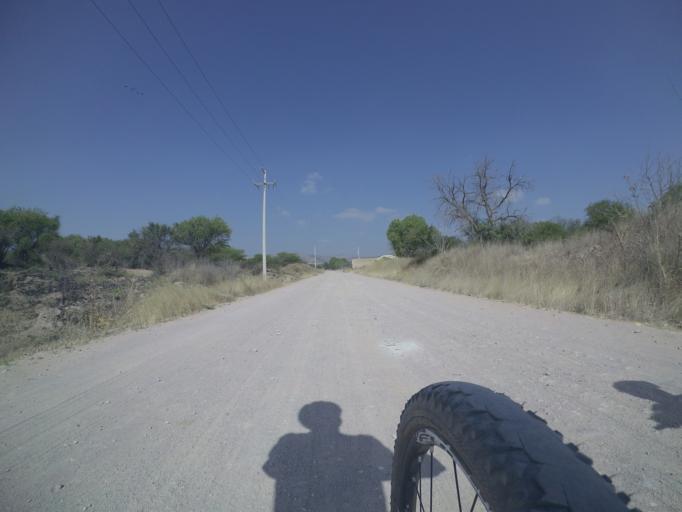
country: MX
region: Aguascalientes
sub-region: Jesus Maria
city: Paseos de las Haciendas [Fraccionamiento]
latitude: 21.9991
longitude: -102.3419
